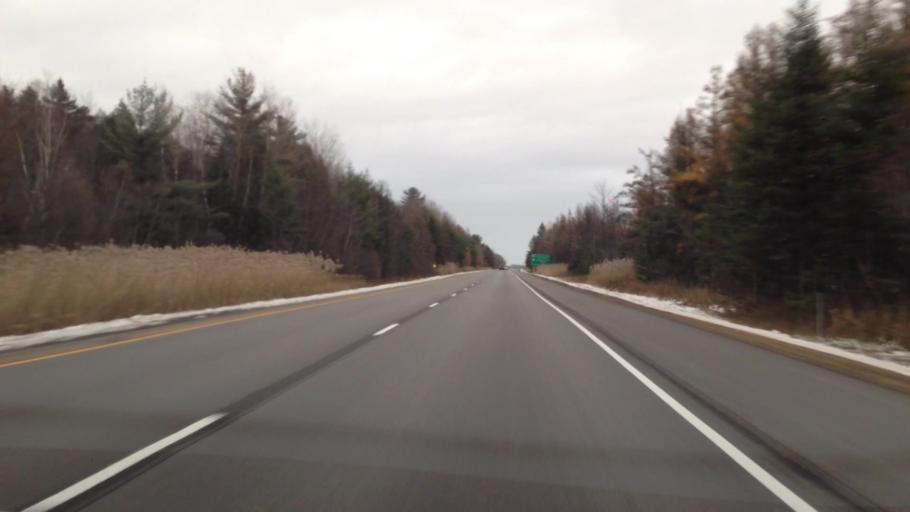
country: CA
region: Quebec
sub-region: Laurentides
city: Brownsburg-Chatham
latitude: 45.5589
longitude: -74.4730
